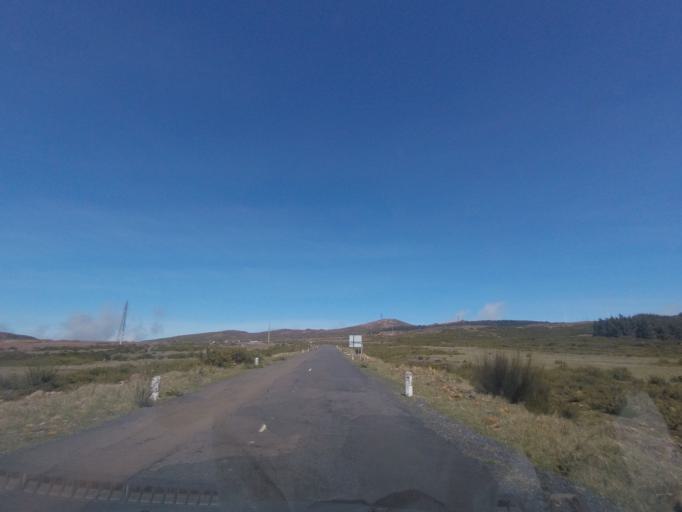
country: PT
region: Madeira
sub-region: Calheta
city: Arco da Calheta
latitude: 32.7554
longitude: -17.0977
